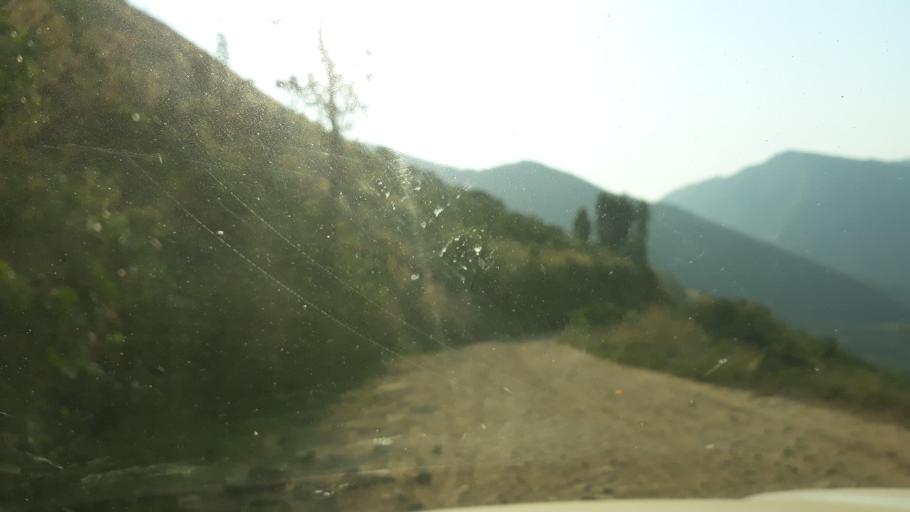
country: RW
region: Western Province
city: Cyangugu
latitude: -2.7080
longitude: 28.9654
